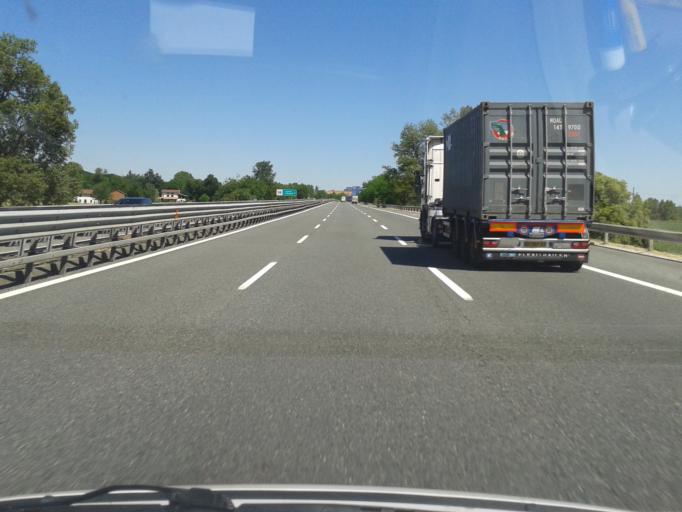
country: IT
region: Piedmont
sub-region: Provincia di Alessandria
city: Silvano d'Orba
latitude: 44.7079
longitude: 8.6676
